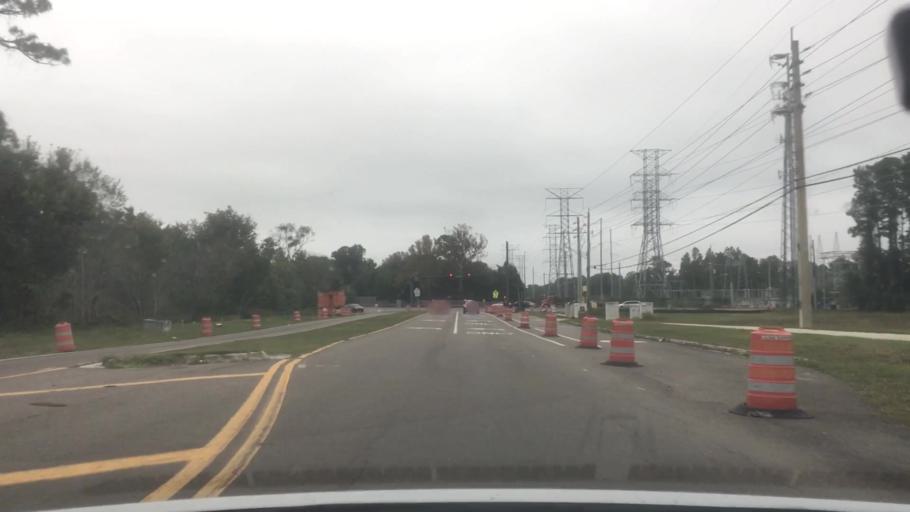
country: US
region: Florida
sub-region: Duval County
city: Atlantic Beach
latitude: 30.3581
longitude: -81.4901
